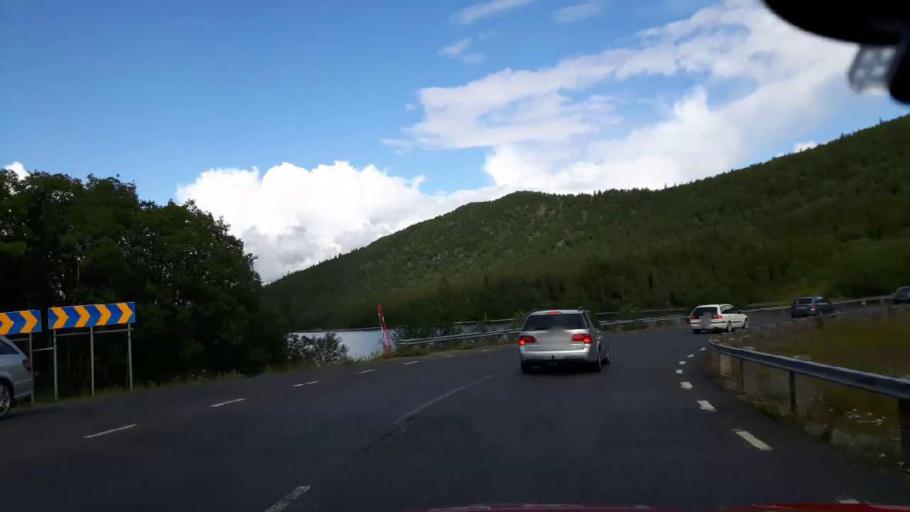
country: SE
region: Vaesterbotten
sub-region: Vilhelmina Kommun
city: Sjoberg
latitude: 65.0305
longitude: 15.1388
